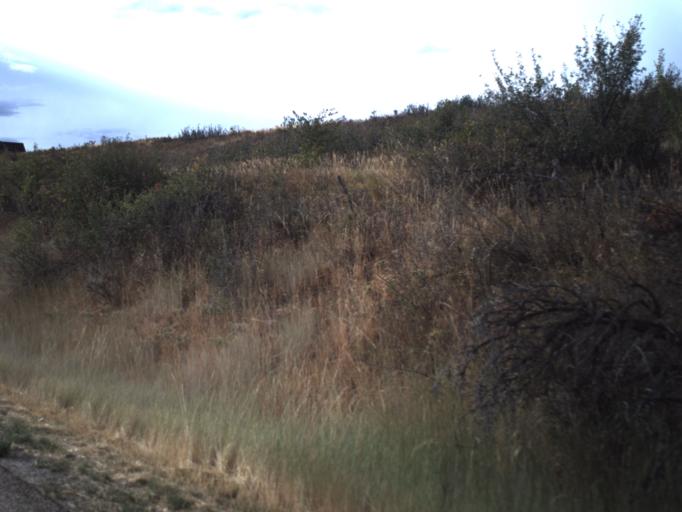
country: US
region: Utah
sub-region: Morgan County
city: Morgan
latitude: 40.9635
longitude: -111.6705
